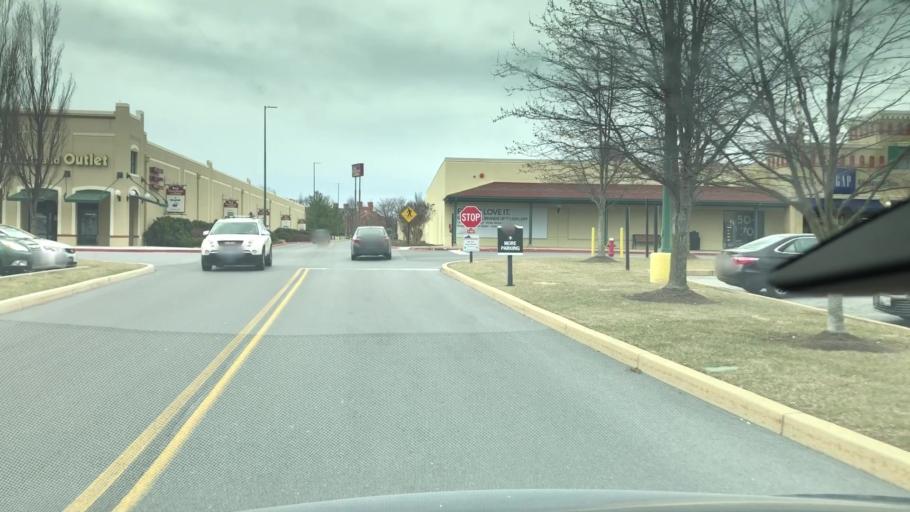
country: US
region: Maryland
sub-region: Washington County
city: Halfway
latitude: 39.6082
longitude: -77.7317
